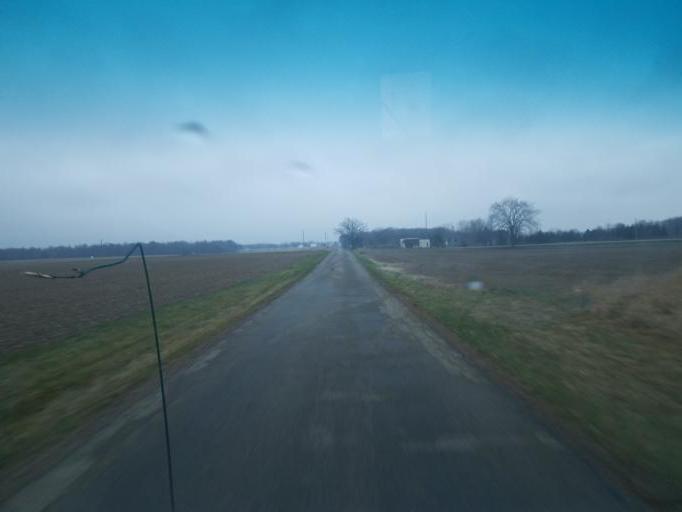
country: US
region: Ohio
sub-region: Defiance County
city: Hicksville
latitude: 41.3391
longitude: -84.7503
